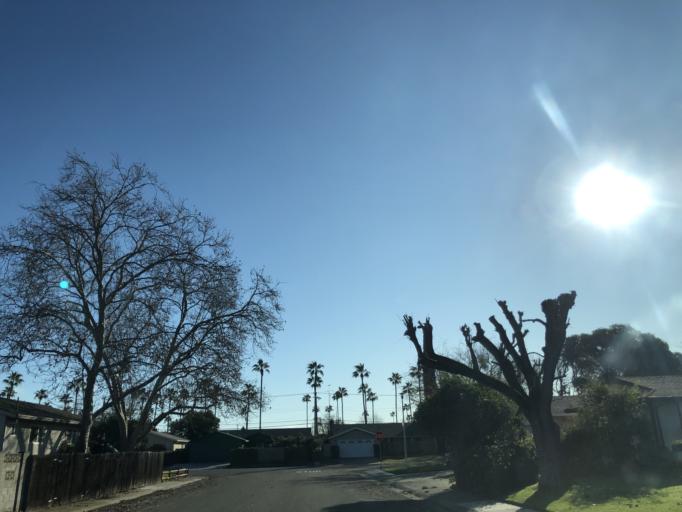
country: US
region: California
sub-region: Sacramento County
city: Rosemont
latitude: 38.5514
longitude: -121.4034
